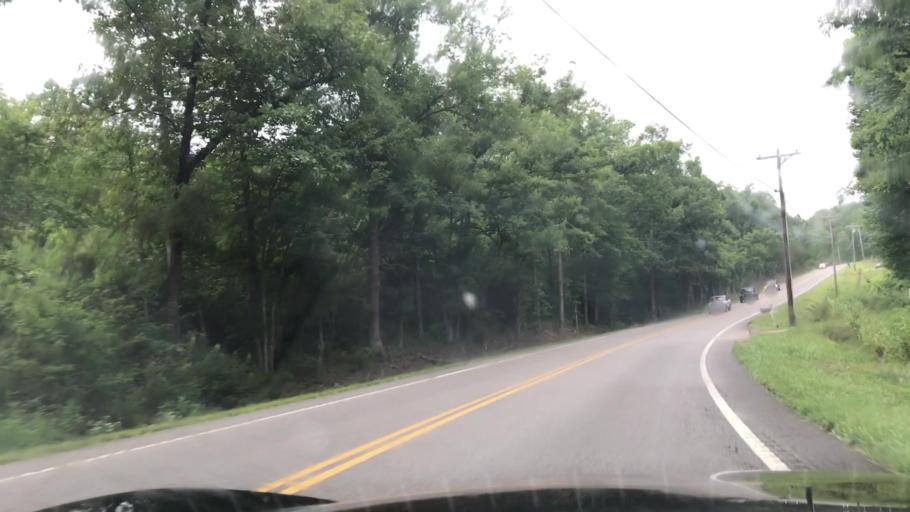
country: US
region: Tennessee
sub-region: Putnam County
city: Monterey
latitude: 36.1310
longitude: -85.2065
